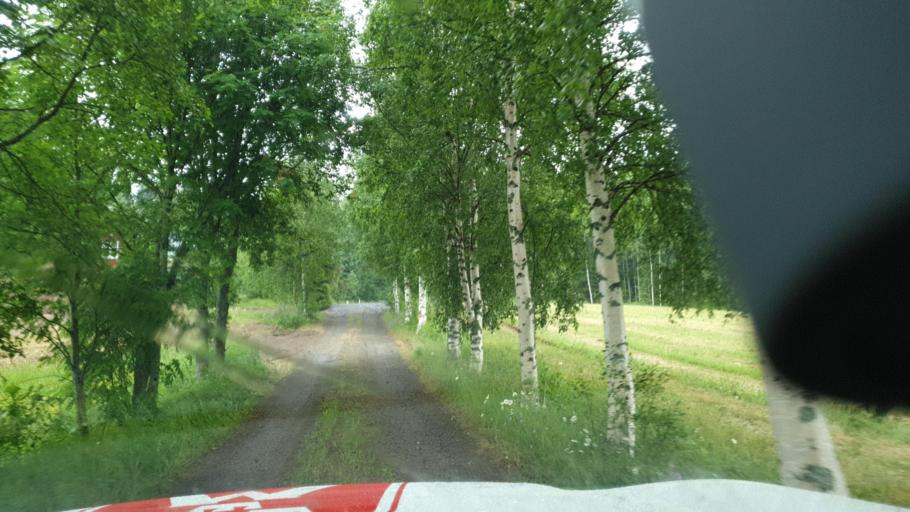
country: SE
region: Vaesterbotten
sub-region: Vannas Kommun
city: Vaennaes
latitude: 63.7604
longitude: 19.6368
